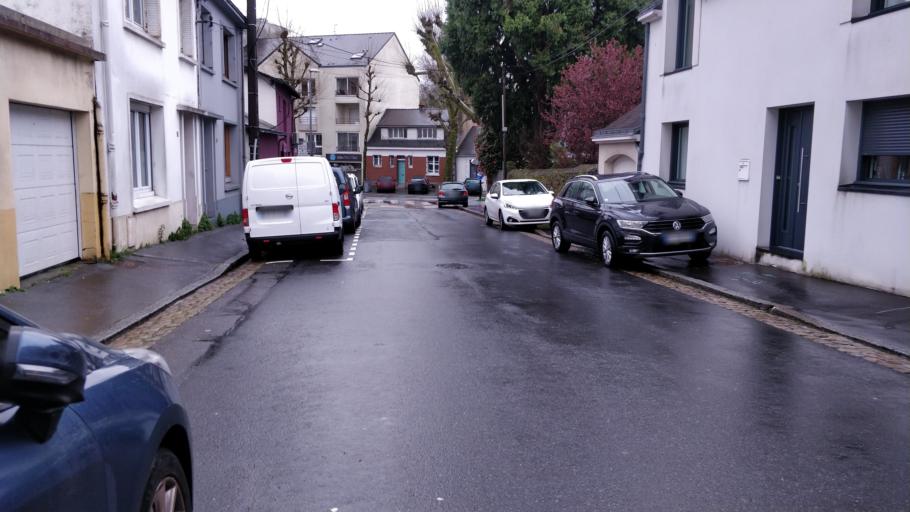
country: FR
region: Pays de la Loire
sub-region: Departement de la Loire-Atlantique
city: Nantes
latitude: 47.2348
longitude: -1.5455
